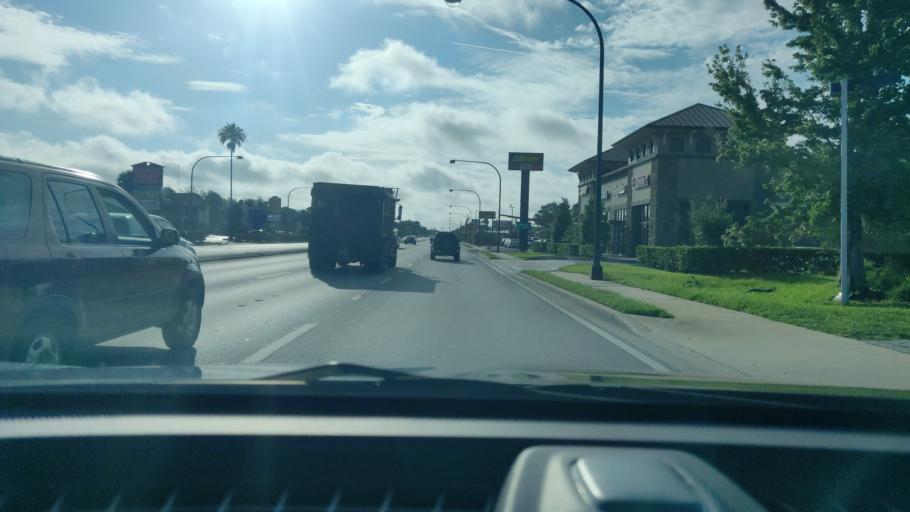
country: US
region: Florida
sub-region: Osceola County
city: Kissimmee
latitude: 28.3044
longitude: -81.4240
